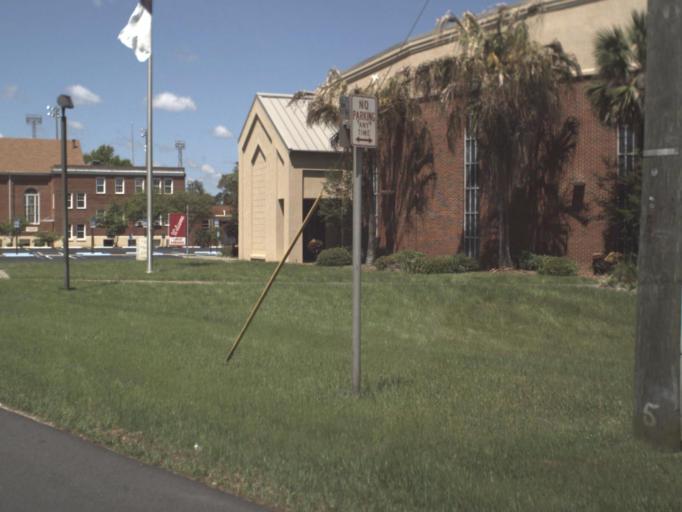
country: US
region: Florida
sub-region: Escambia County
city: Myrtle Grove
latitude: 30.4249
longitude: -87.2945
